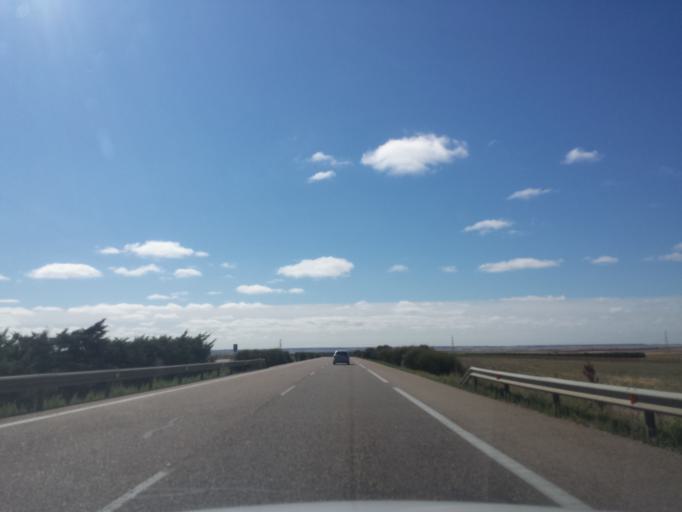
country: ES
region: Castille and Leon
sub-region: Provincia de Zamora
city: Quintanilla del Monte
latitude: 41.8137
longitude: -5.3614
